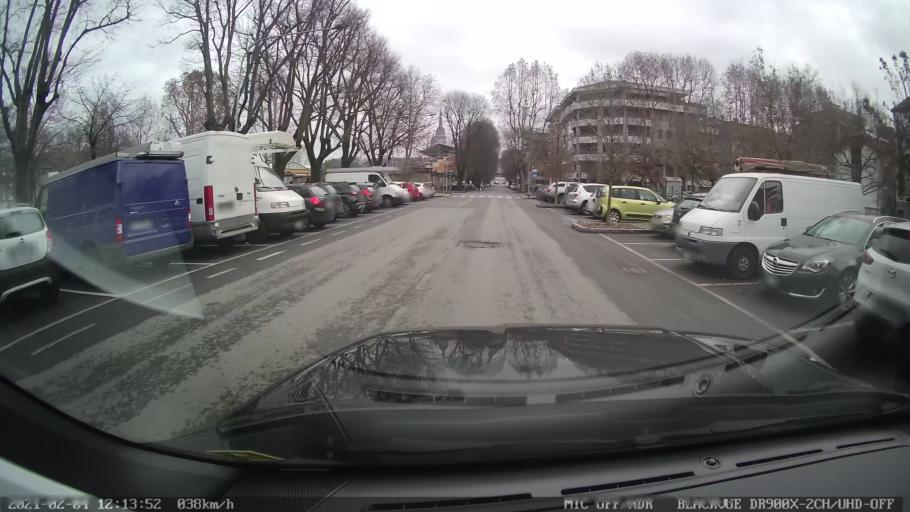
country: IT
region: Piedmont
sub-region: Provincia di Novara
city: Novara
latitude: 45.4479
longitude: 8.6106
